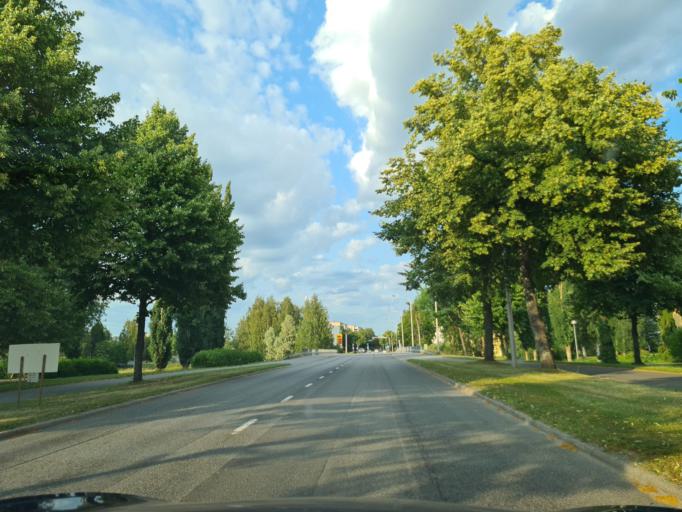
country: FI
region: Southern Ostrobothnia
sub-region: Seinaejoki
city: Lapua
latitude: 62.9708
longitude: 22.9985
